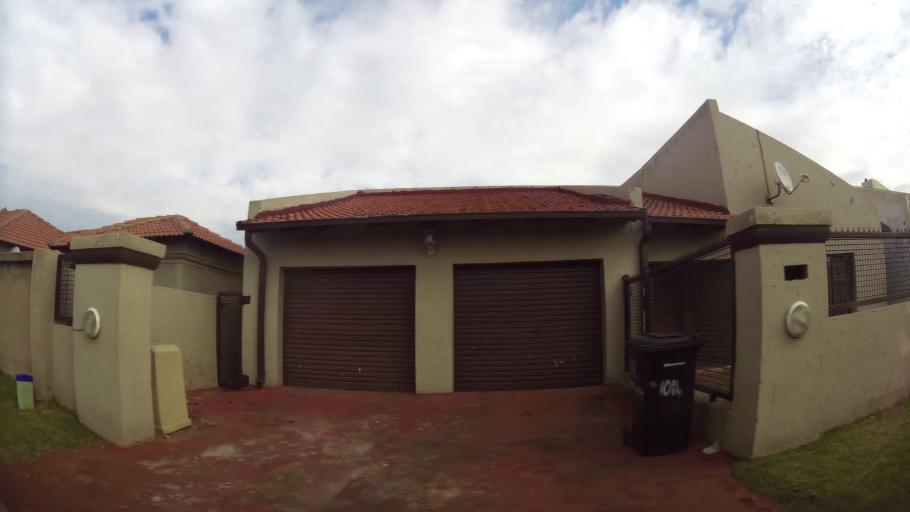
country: ZA
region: Gauteng
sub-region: Ekurhuleni Metropolitan Municipality
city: Germiston
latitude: -26.3230
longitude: 28.1781
